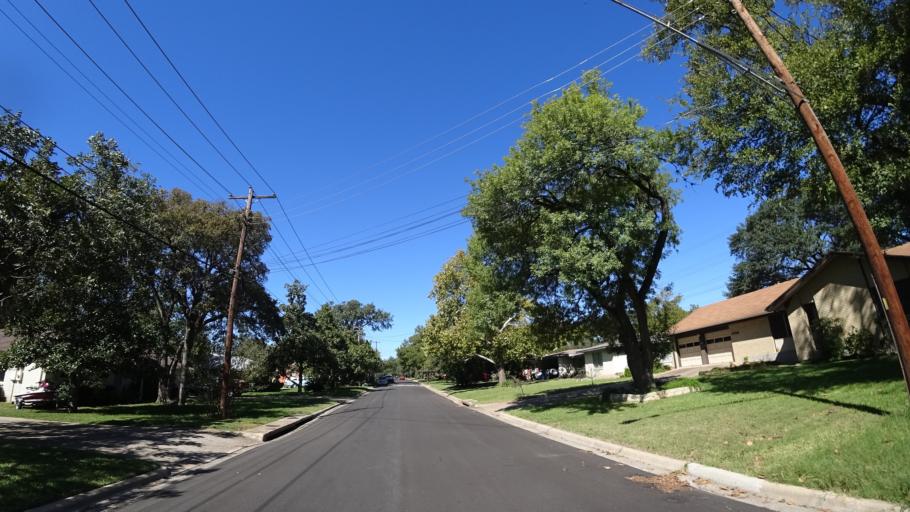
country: US
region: Texas
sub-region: Travis County
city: Rollingwood
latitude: 30.2247
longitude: -97.7938
